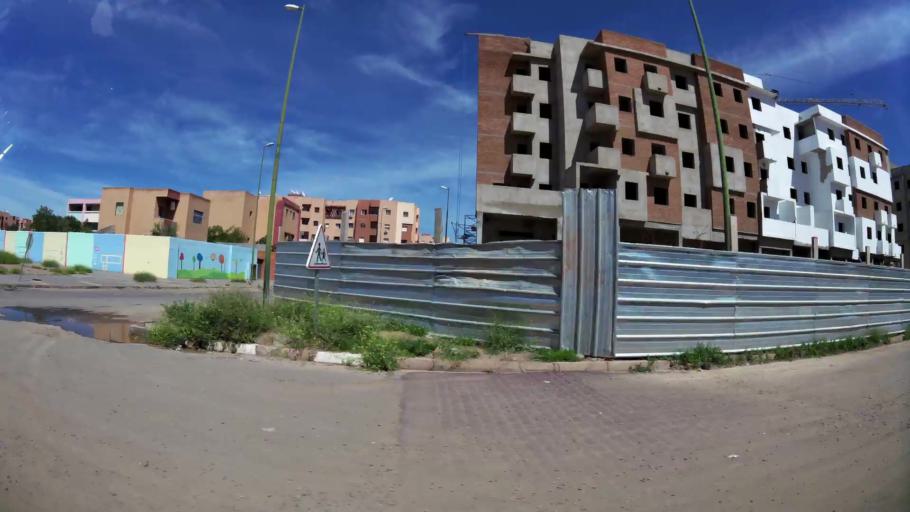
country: MA
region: Marrakech-Tensift-Al Haouz
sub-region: Marrakech
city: Marrakesh
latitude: 31.6352
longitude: -8.0745
